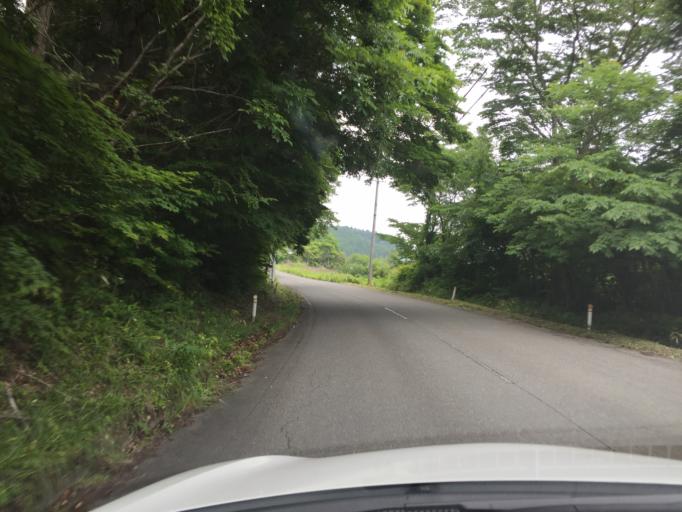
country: JP
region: Fukushima
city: Iwaki
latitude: 37.1739
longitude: 140.7134
